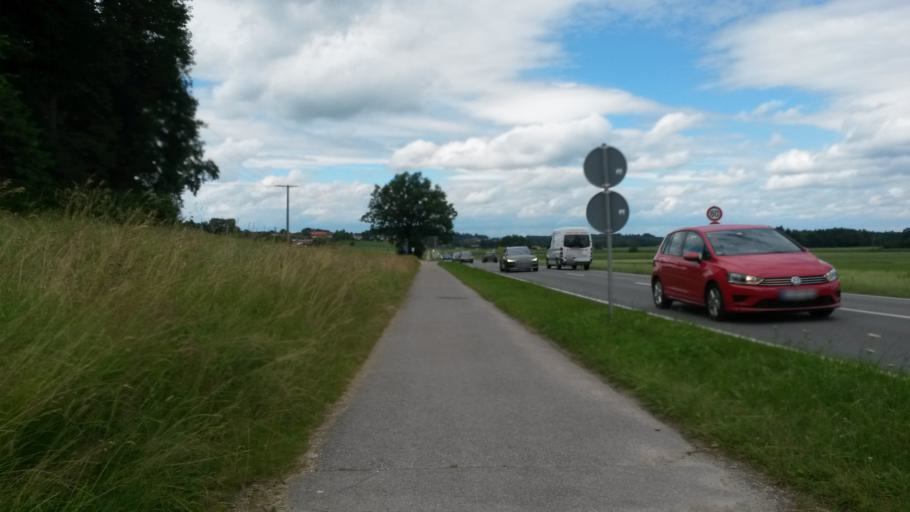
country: DE
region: Bavaria
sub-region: Upper Bavaria
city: Bernau am Chiemsee
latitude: 47.8186
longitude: 12.3623
